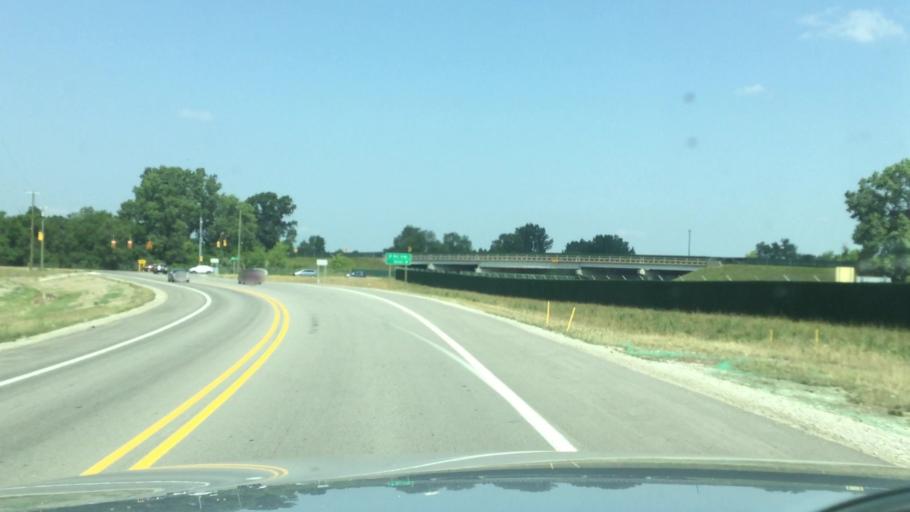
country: US
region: Michigan
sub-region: Washtenaw County
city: Ypsilanti
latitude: 42.2406
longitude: -83.5651
